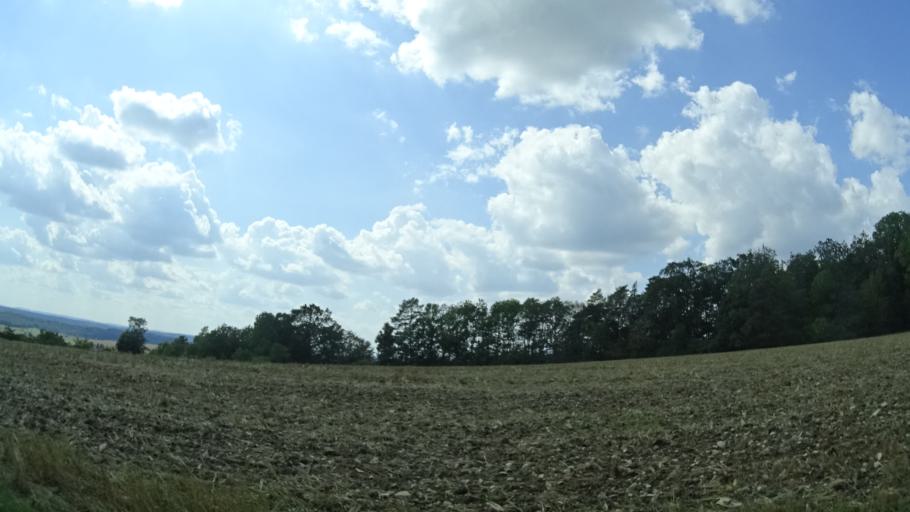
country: DE
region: Thuringia
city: Hildburghausen
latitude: 50.3812
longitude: 10.7455
